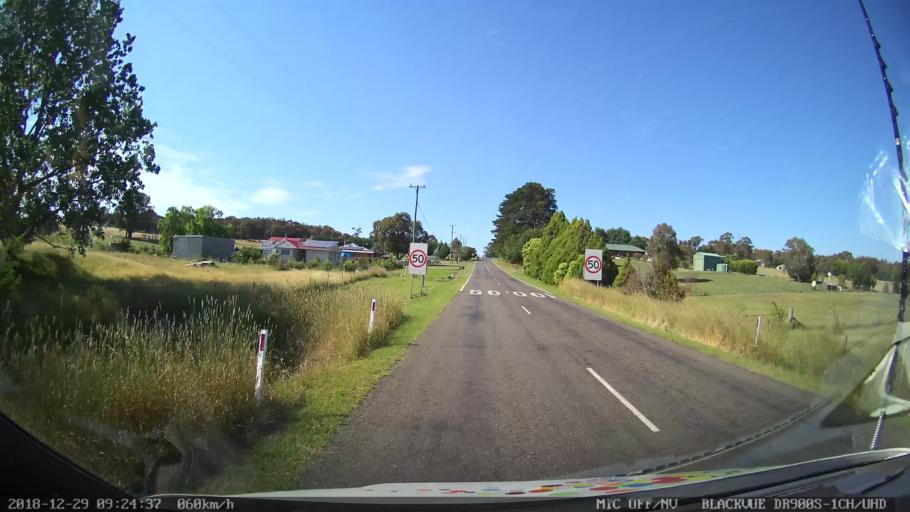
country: AU
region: New South Wales
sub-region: Upper Lachlan Shire
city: Crookwell
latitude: -34.5380
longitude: 149.3939
